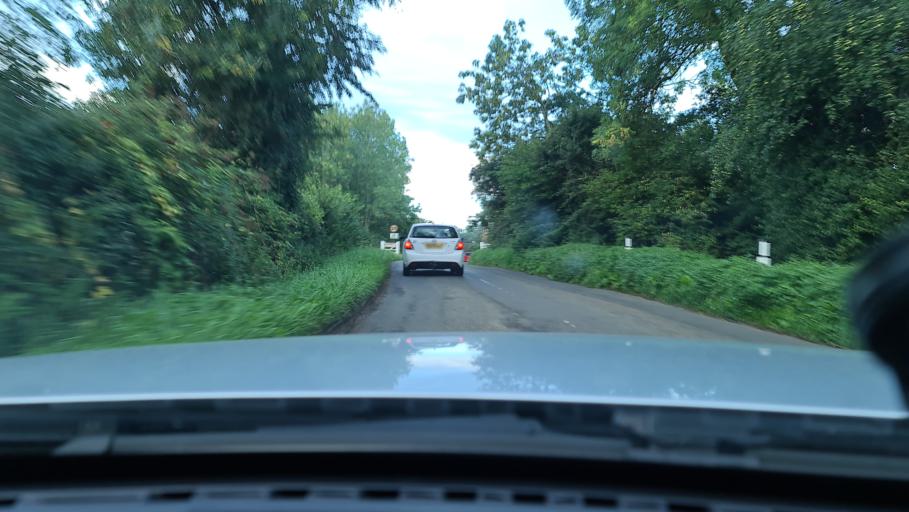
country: GB
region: England
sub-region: Oxfordshire
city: Hanwell
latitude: 52.0923
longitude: -1.3601
